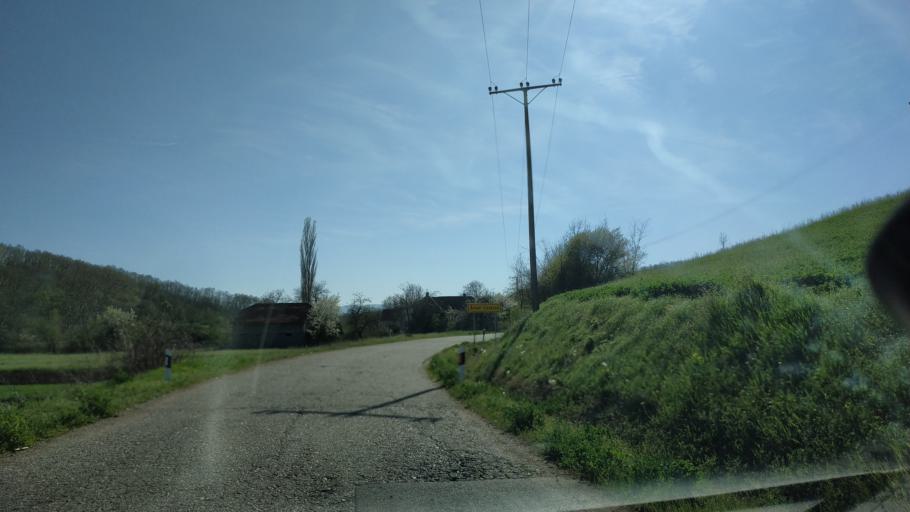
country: RS
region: Central Serbia
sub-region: Nisavski Okrug
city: Aleksinac
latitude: 43.4895
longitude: 21.6648
